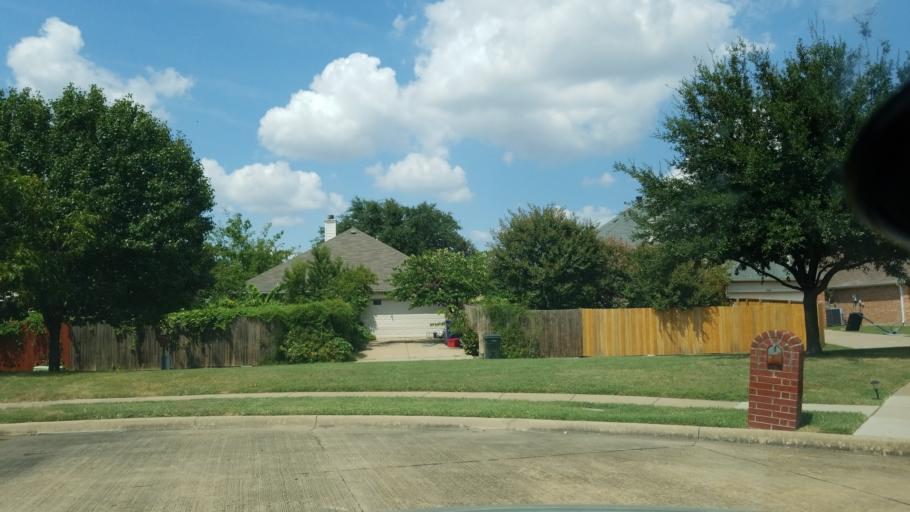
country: US
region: Texas
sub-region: Dallas County
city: Garland
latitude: 32.9273
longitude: -96.6625
